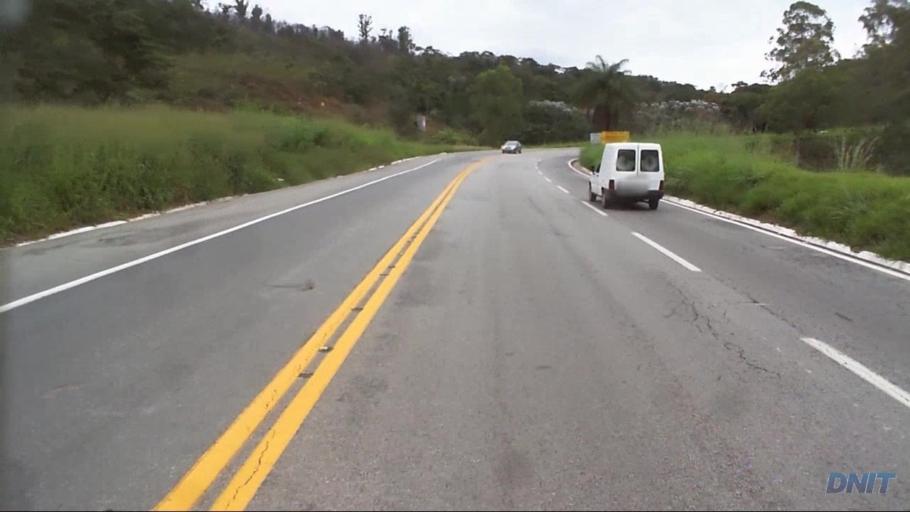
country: BR
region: Minas Gerais
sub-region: Joao Monlevade
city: Joao Monlevade
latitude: -19.8522
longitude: -43.2711
